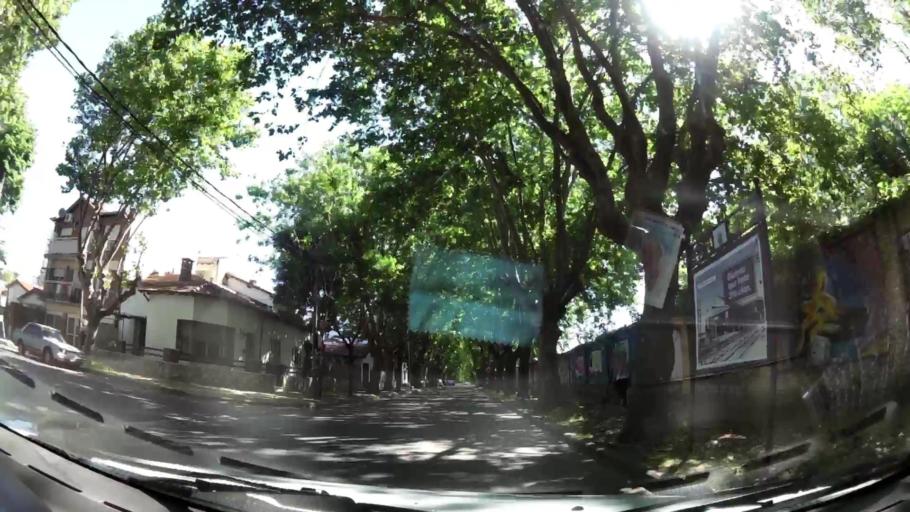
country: AR
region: Buenos Aires
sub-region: Partido de San Isidro
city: San Isidro
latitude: -34.4668
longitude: -58.5257
